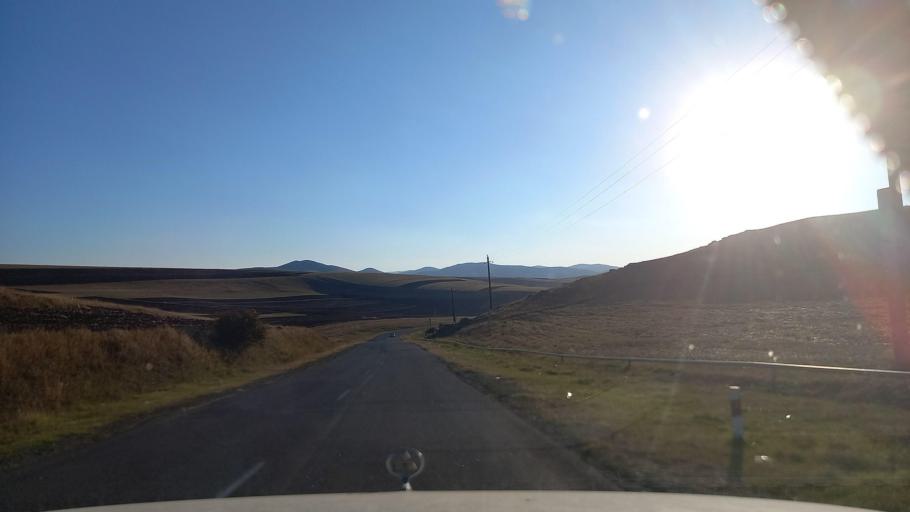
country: AZ
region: Shamkir Rayon
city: Shamkhor
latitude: 40.7655
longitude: 45.9356
